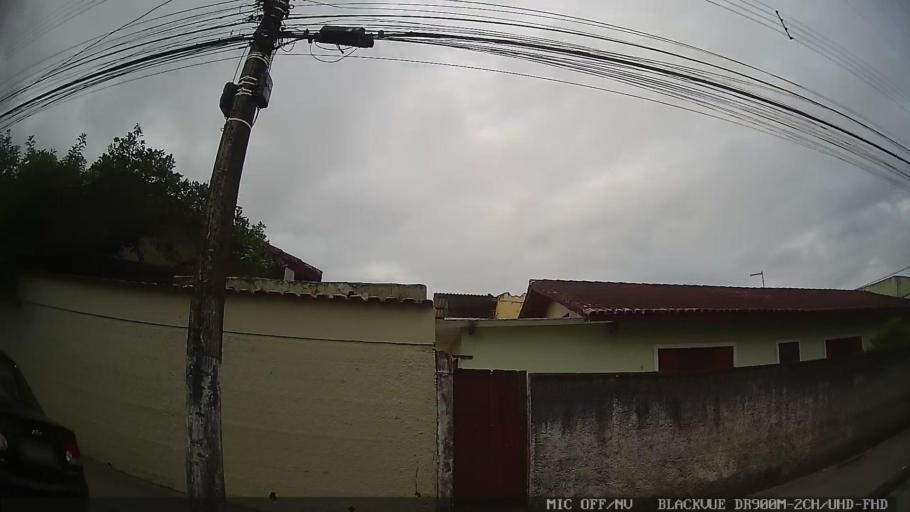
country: BR
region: Sao Paulo
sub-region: Itanhaem
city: Itanhaem
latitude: -24.1914
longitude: -46.8118
